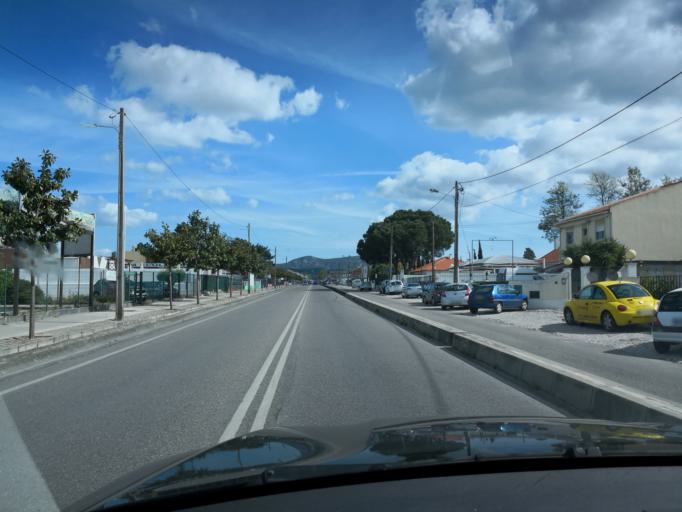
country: PT
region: Setubal
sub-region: Barreiro
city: Santo Antonio da Charneca
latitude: 38.5428
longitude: -9.0279
